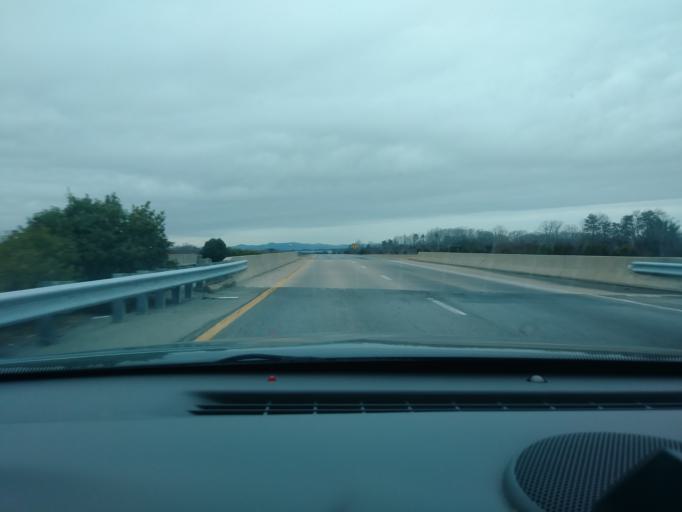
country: US
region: North Carolina
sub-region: Yadkin County
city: Jonesville
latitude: 36.1191
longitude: -80.7930
